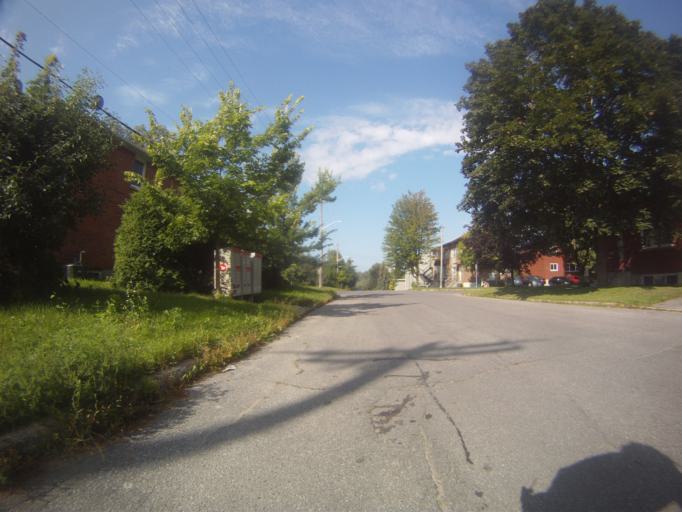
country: CA
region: Ontario
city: Ottawa
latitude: 45.3762
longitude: -75.6749
